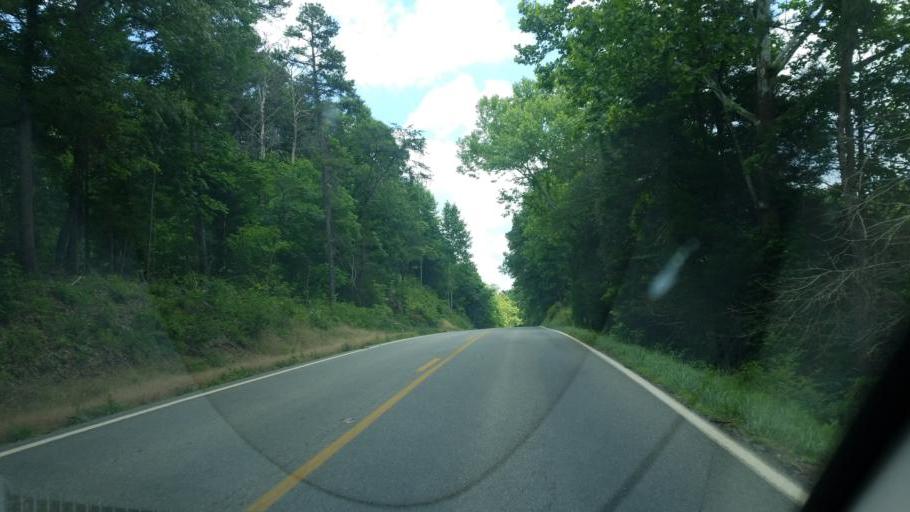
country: US
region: Virginia
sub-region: Appomattox County
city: Appomattox
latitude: 37.5228
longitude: -78.7566
